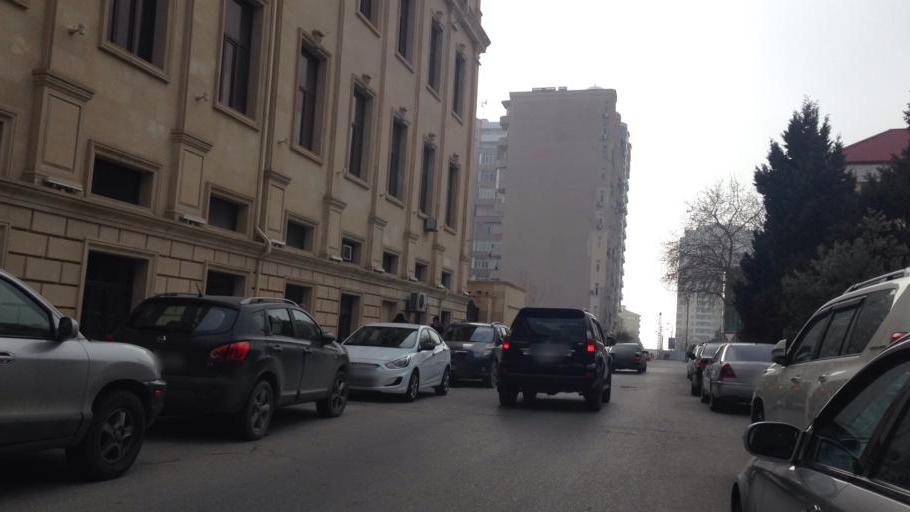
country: AZ
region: Baki
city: Baku
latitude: 40.3819
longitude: 49.8715
